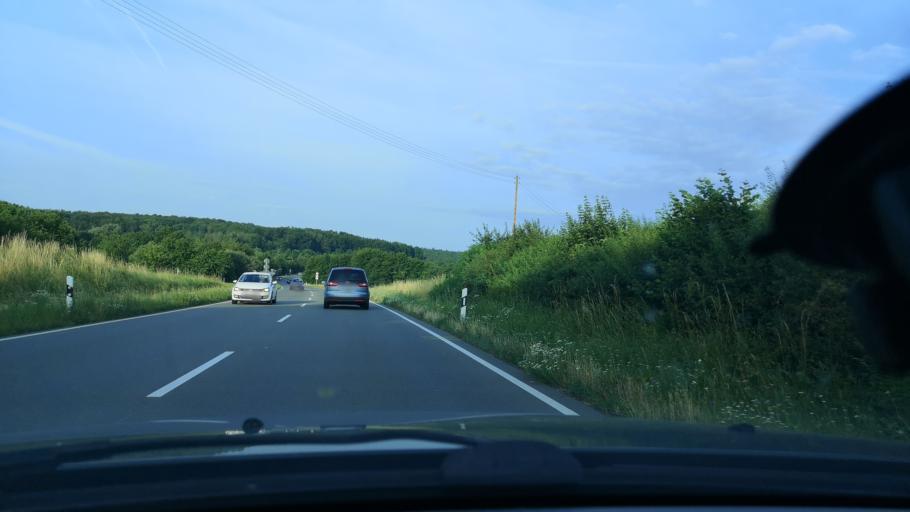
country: DE
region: Baden-Wuerttemberg
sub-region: Regierungsbezirk Stuttgart
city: Schlierbach
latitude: 48.6716
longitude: 9.5080
